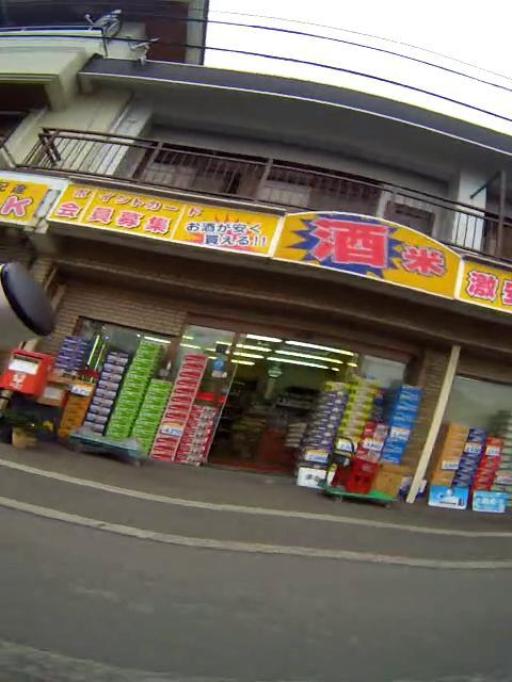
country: JP
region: Hyogo
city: Fukura
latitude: 34.2775
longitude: 134.7663
